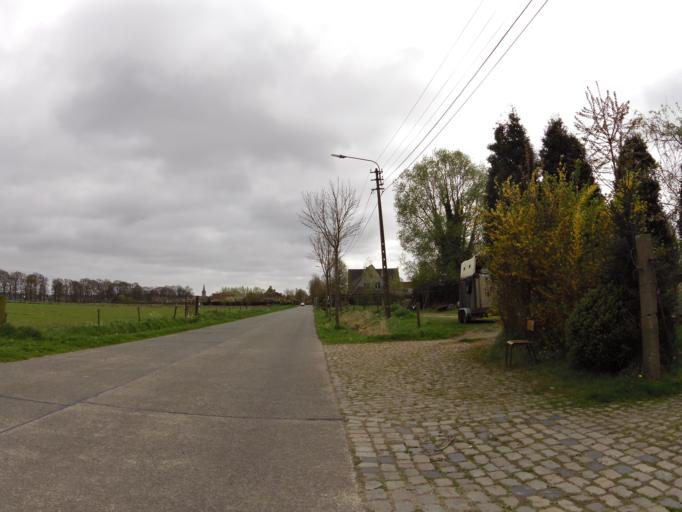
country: BE
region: Flanders
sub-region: Provincie West-Vlaanderen
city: Jabbeke
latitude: 51.1957
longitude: 3.1346
